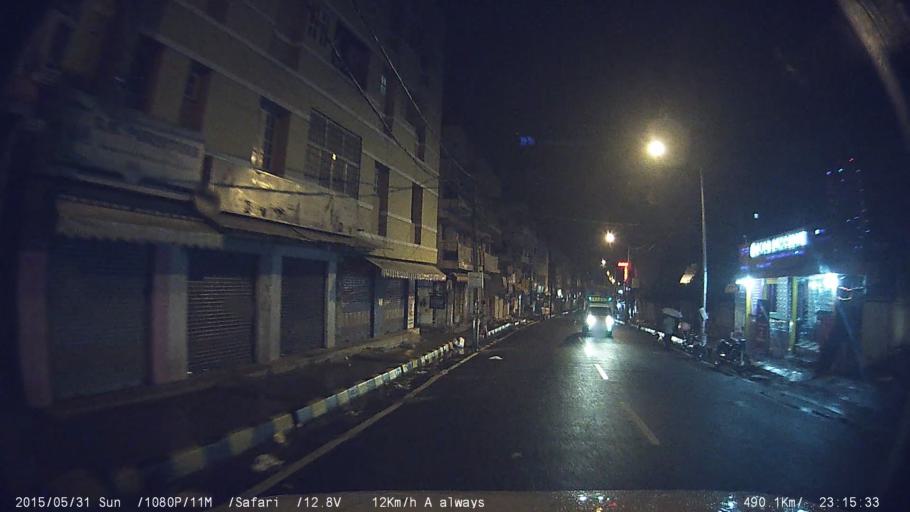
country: IN
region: Karnataka
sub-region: Bangalore Urban
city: Bangalore
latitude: 12.9198
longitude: 77.6129
